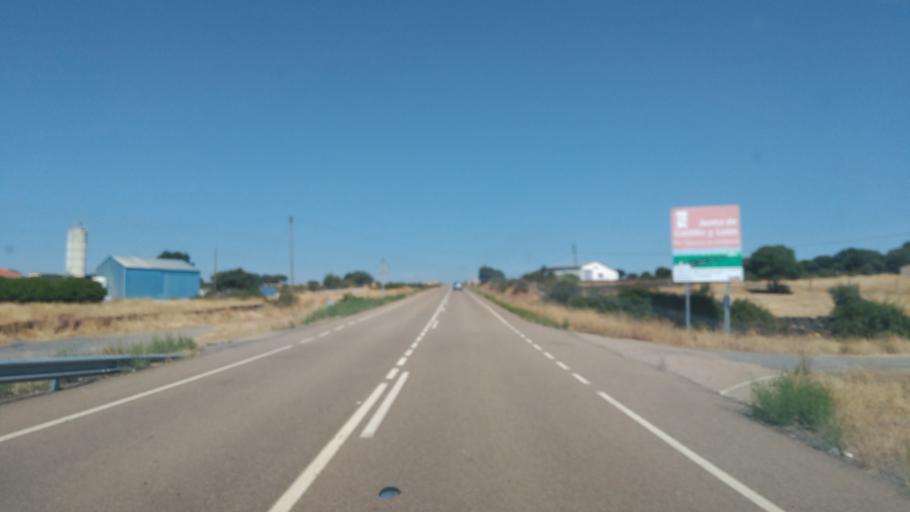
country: ES
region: Castille and Leon
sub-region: Provincia de Salamanca
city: Aldeanueva de la Sierra
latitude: 40.6175
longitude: -6.1009
